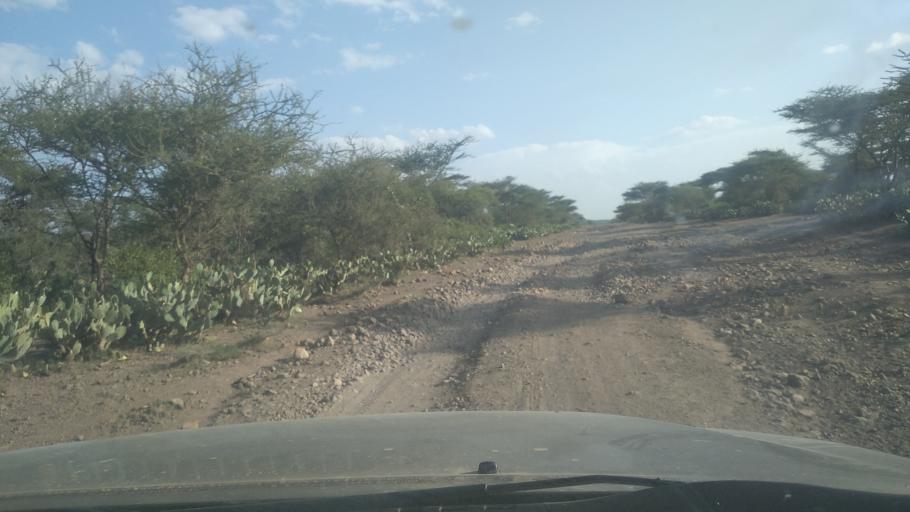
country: ET
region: Oromiya
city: Hirna
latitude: 9.4165
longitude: 40.9595
